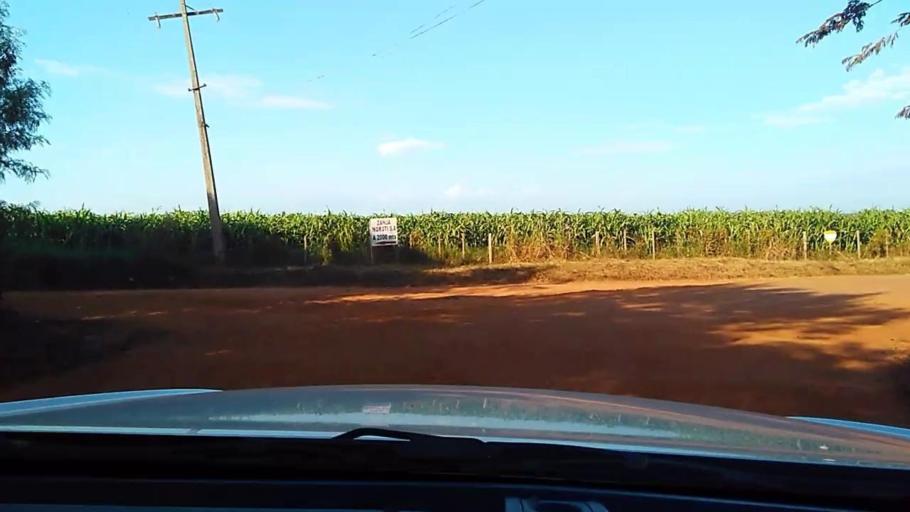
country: PY
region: Alto Parana
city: Doctor Juan Leon Mallorquin
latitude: -25.6961
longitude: -55.3791
